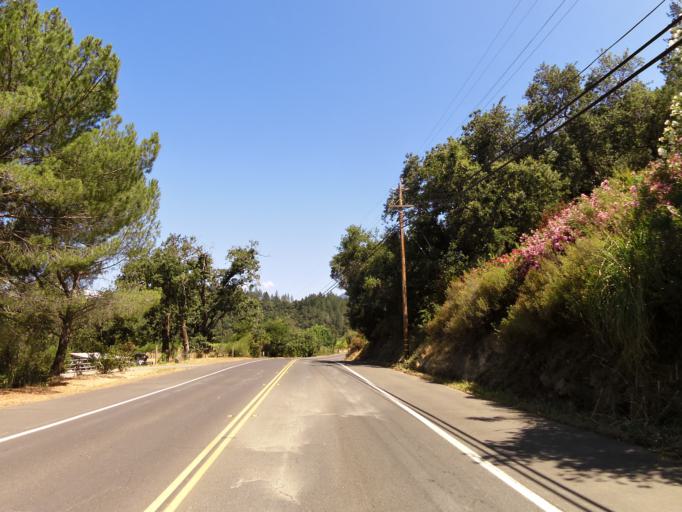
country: US
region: California
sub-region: Napa County
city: Deer Park
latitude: 38.5396
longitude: -122.4896
